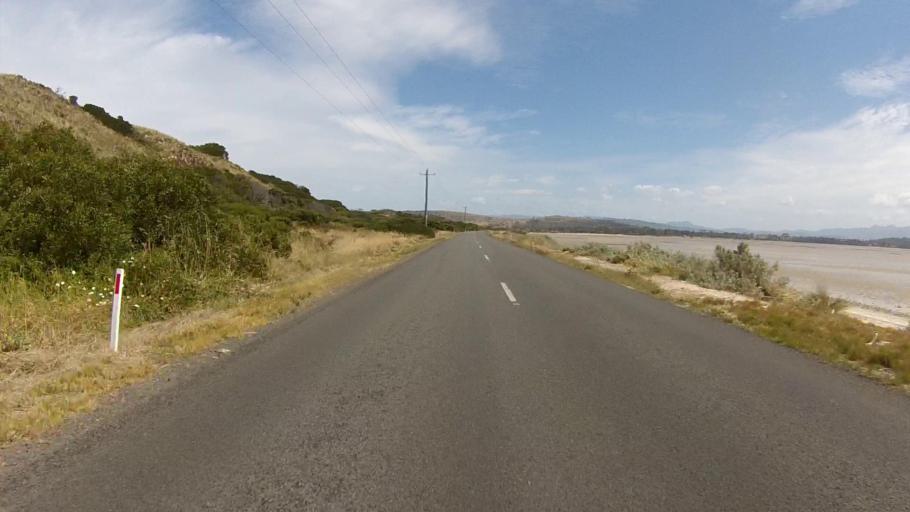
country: AU
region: Tasmania
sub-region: Clarence
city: Sandford
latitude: -43.0317
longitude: 147.4582
